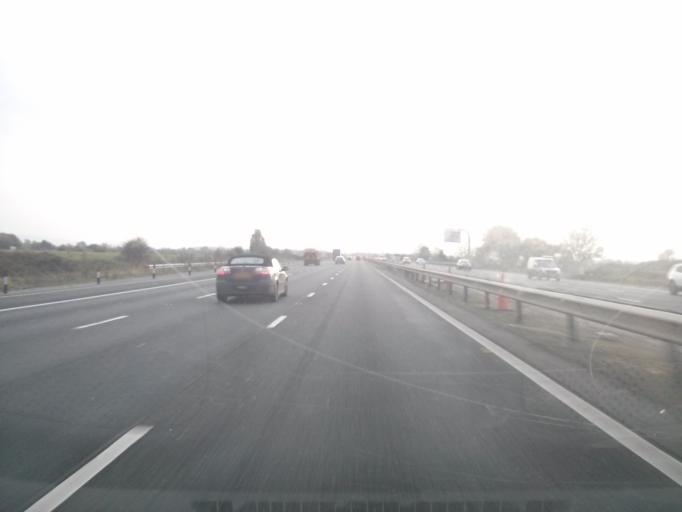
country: GB
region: England
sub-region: Gloucestershire
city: Stonehouse
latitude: 51.7886
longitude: -2.2990
